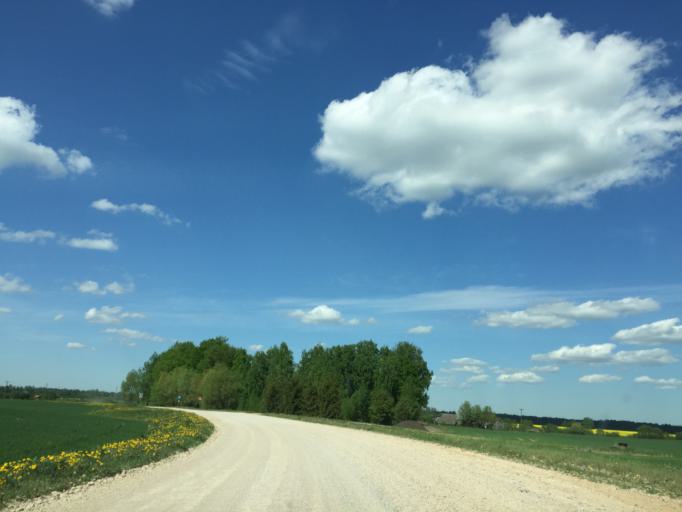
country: LV
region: Rundales
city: Pilsrundale
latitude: 56.3771
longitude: 24.0795
